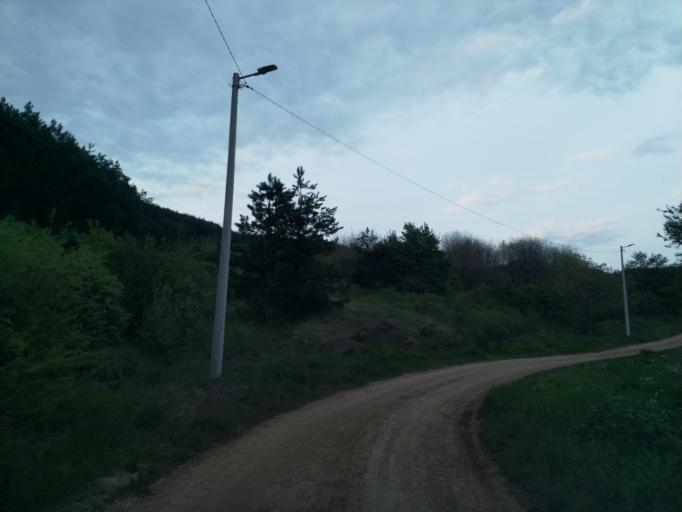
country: RS
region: Central Serbia
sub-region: Pomoravski Okrug
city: Paracin
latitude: 43.9423
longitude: 21.5085
